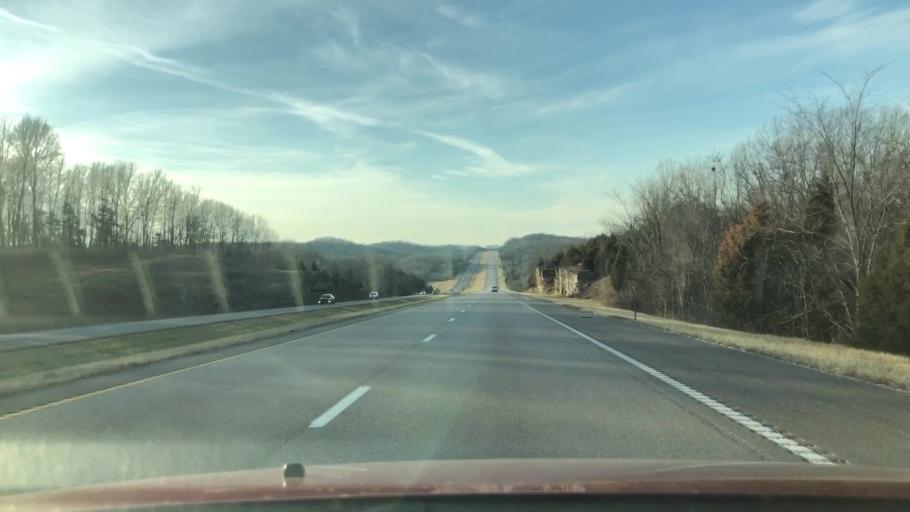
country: US
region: Missouri
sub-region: Wright County
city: Mansfield
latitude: 37.1108
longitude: -92.6467
